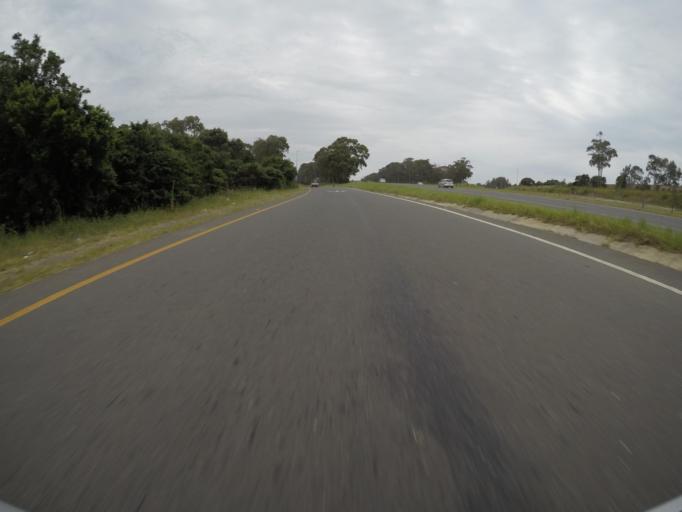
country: ZA
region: Eastern Cape
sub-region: Buffalo City Metropolitan Municipality
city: East London
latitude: -32.9397
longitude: 27.9488
